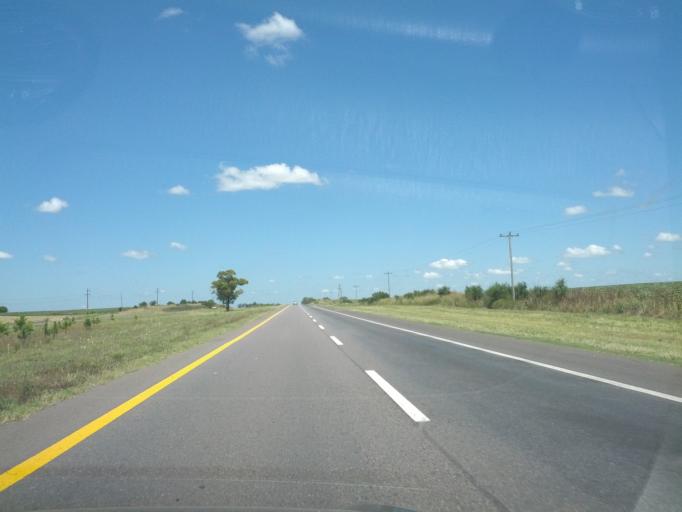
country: AR
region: Entre Rios
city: Gualeguaychu
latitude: -33.0862
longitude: -58.6381
